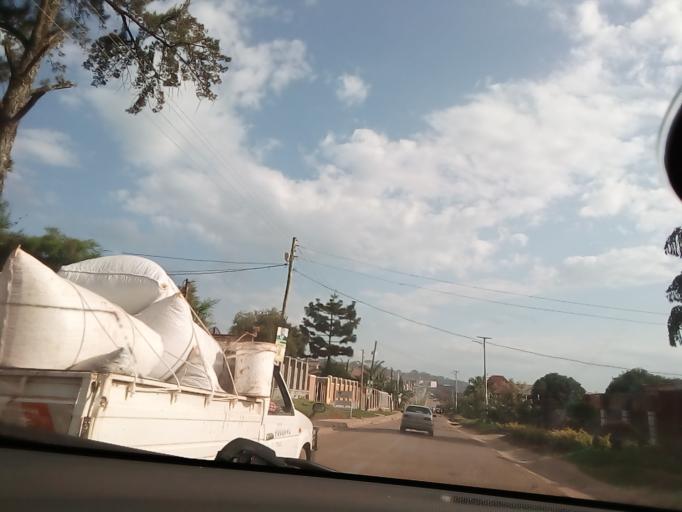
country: UG
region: Central Region
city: Masaka
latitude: -0.3492
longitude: 31.7421
